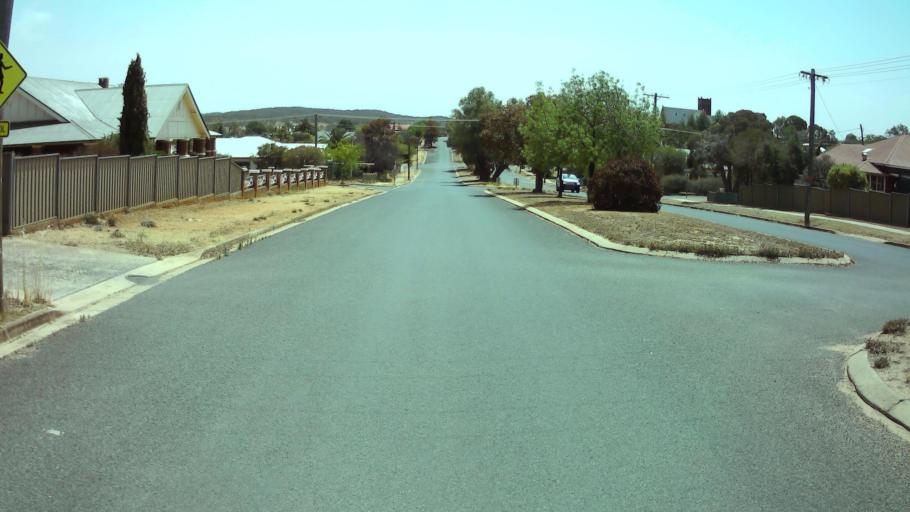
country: AU
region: New South Wales
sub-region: Weddin
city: Grenfell
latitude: -33.8992
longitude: 148.1594
